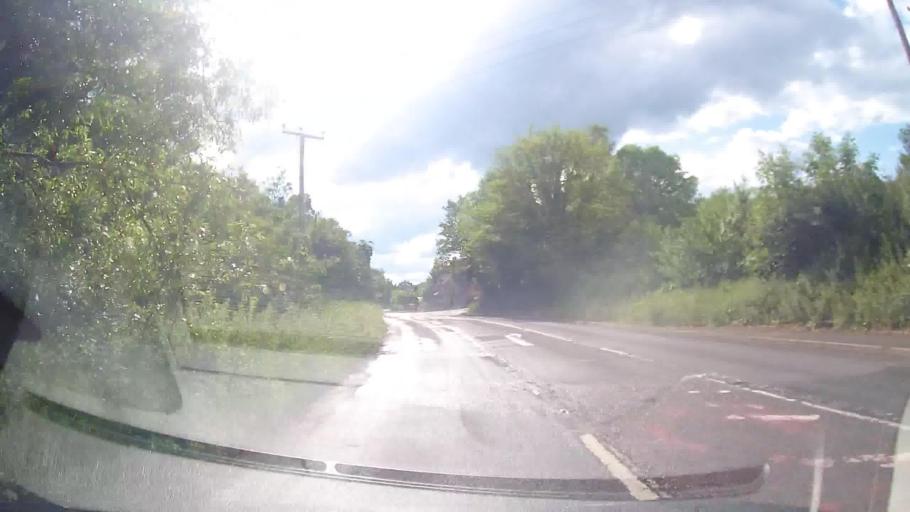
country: GB
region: England
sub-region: Telford and Wrekin
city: Ironbridge
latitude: 52.6376
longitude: -2.5274
